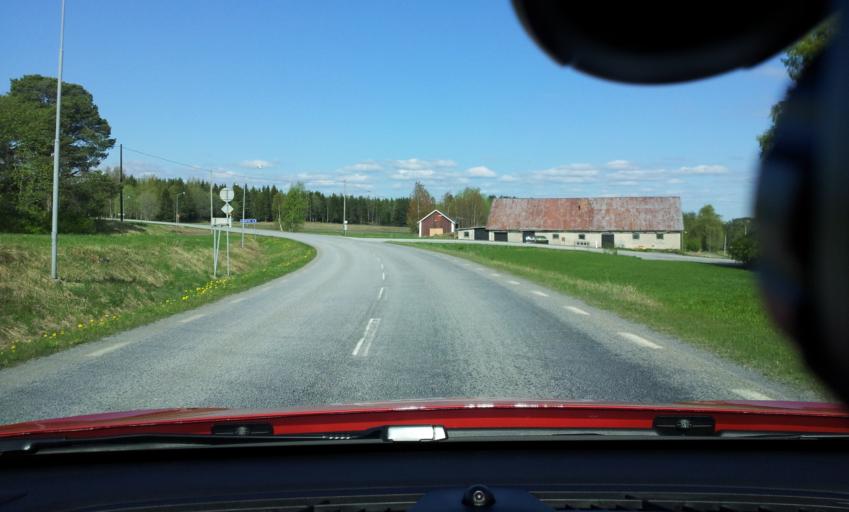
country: SE
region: Jaemtland
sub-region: Krokoms Kommun
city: Krokom
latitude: 63.1347
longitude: 14.2744
